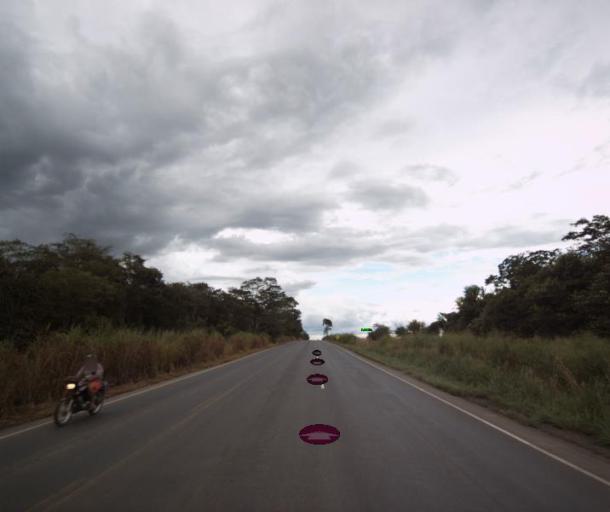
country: BR
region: Goias
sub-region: Itapaci
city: Itapaci
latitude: -14.9926
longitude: -49.4059
